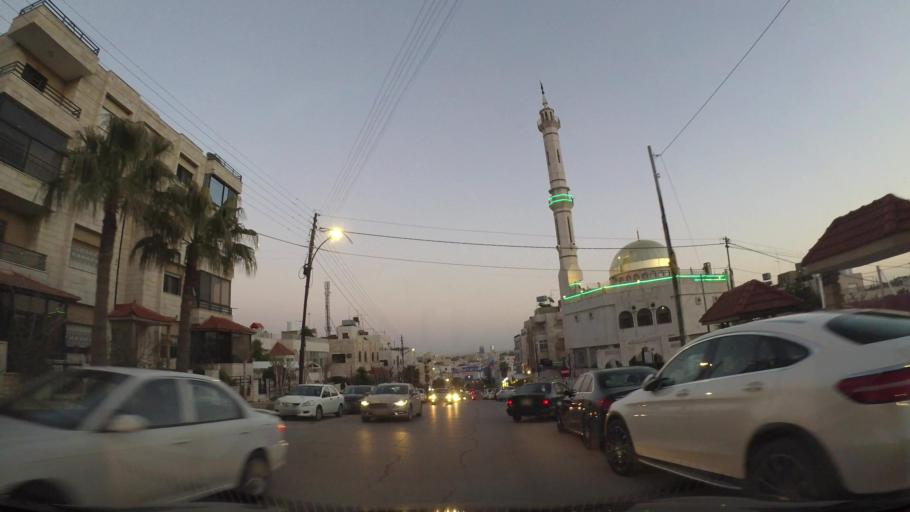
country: JO
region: Amman
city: Al Jubayhah
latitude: 31.9855
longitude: 35.8910
